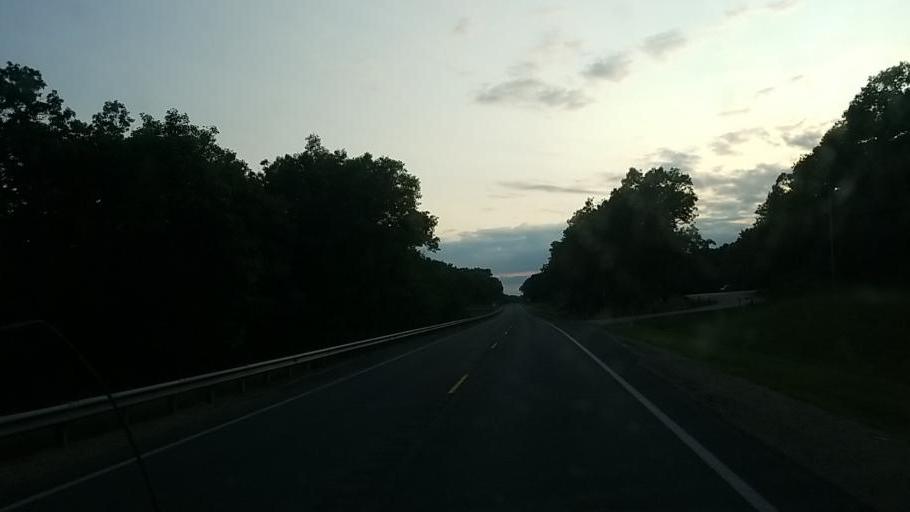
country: US
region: Michigan
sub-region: Newaygo County
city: Newaygo
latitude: 43.4052
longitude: -85.7179
